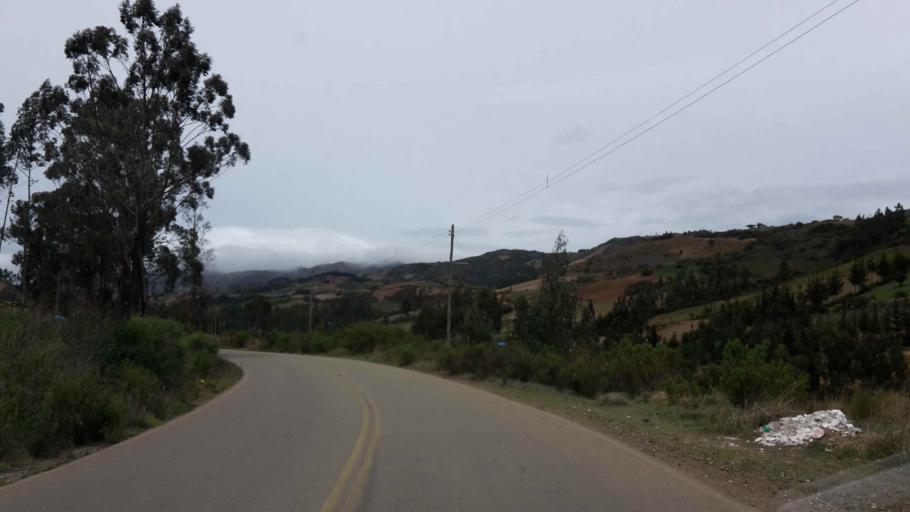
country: BO
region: Cochabamba
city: Totora
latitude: -17.6957
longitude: -65.2142
